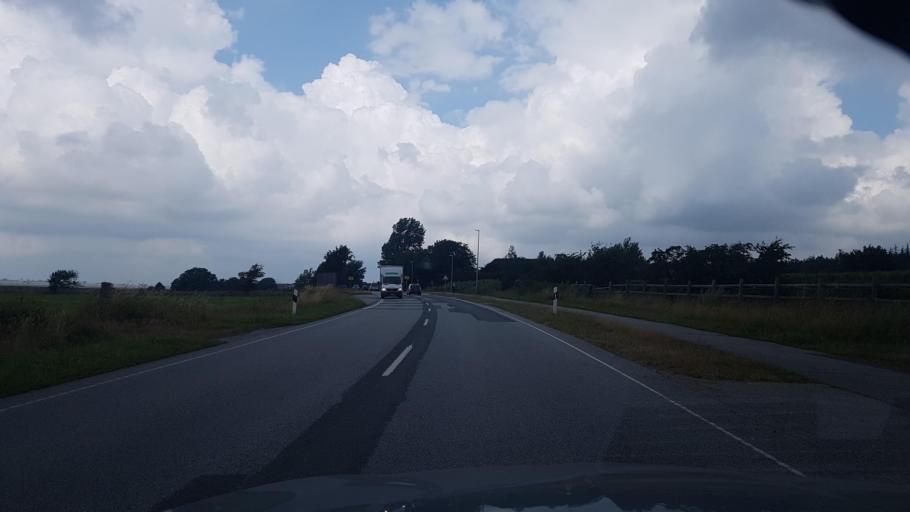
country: DE
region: Schleswig-Holstein
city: Schobull
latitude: 54.5009
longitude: 9.0172
